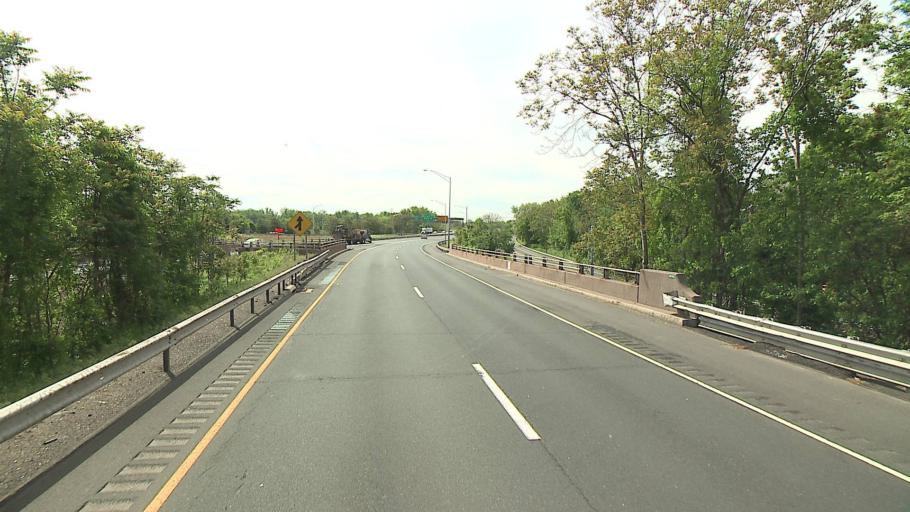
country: US
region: Connecticut
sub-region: Hartford County
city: Hartford
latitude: 41.7640
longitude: -72.6550
